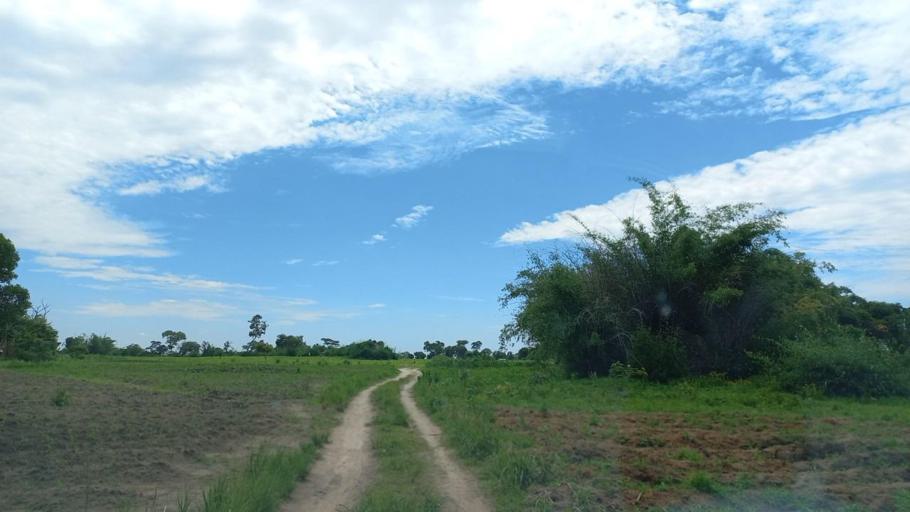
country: ZM
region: Copperbelt
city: Kitwe
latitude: -12.7940
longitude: 28.4006
